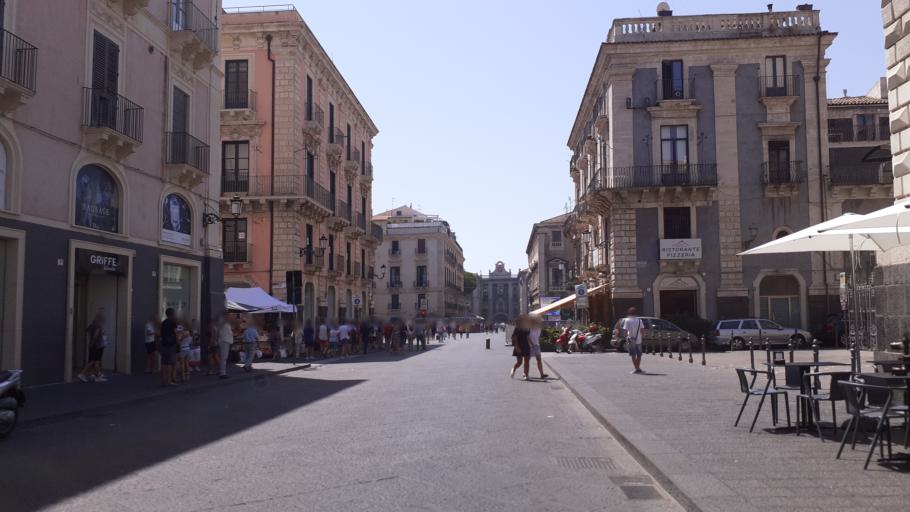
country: IT
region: Sicily
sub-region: Catania
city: Catania
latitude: 37.5045
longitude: 15.0869
